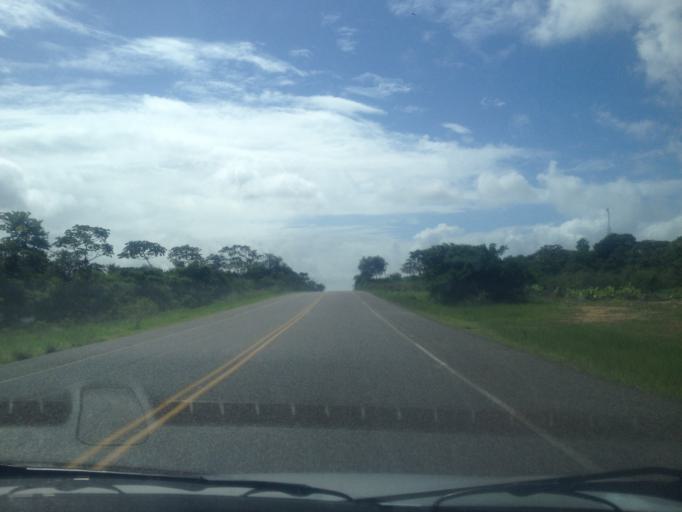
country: BR
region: Bahia
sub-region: Conde
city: Conde
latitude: -11.8055
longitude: -37.6302
